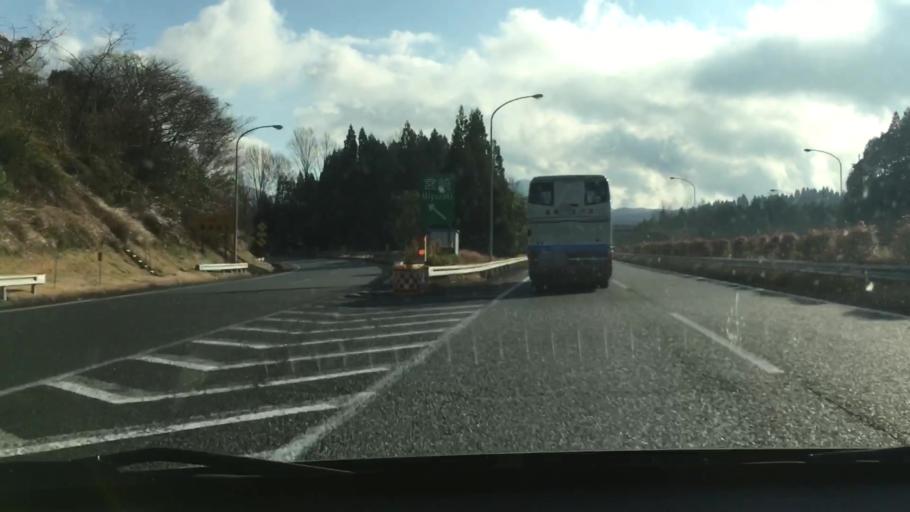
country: JP
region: Kagoshima
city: Okuchi-shinohara
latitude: 32.0355
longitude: 130.7990
